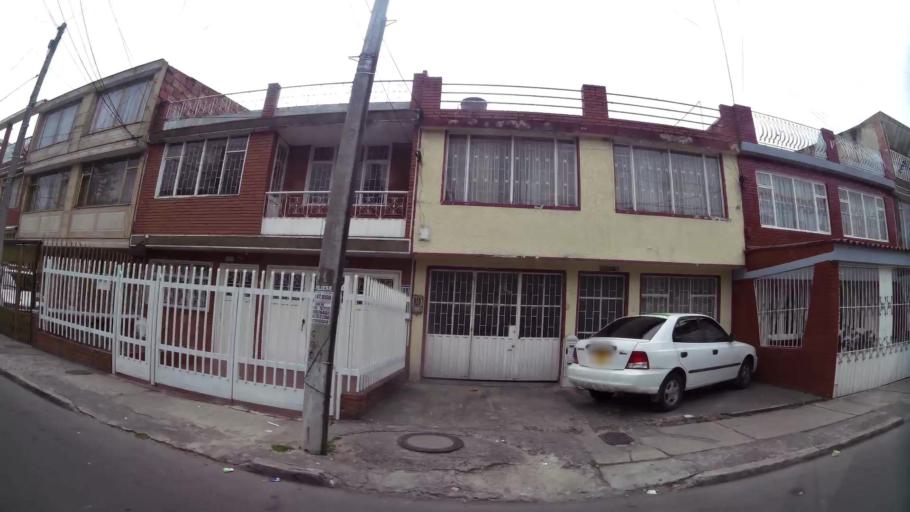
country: CO
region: Bogota D.C.
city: Bogota
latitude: 4.6188
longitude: -74.1113
